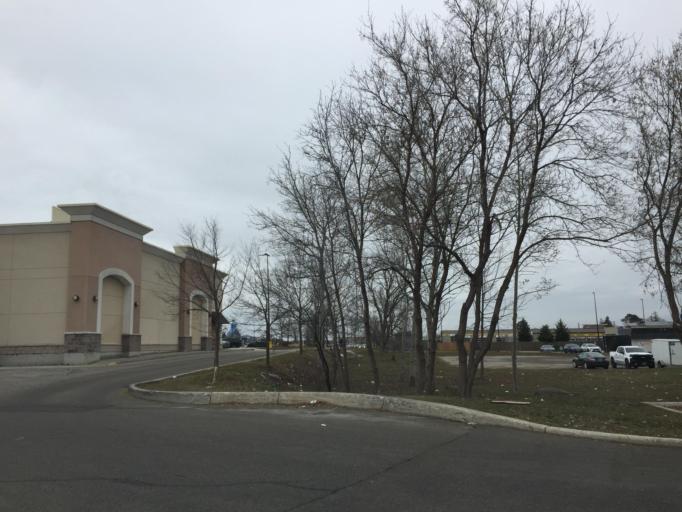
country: CA
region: Ontario
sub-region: Wellington County
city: Guelph
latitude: 43.5626
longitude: -80.2828
